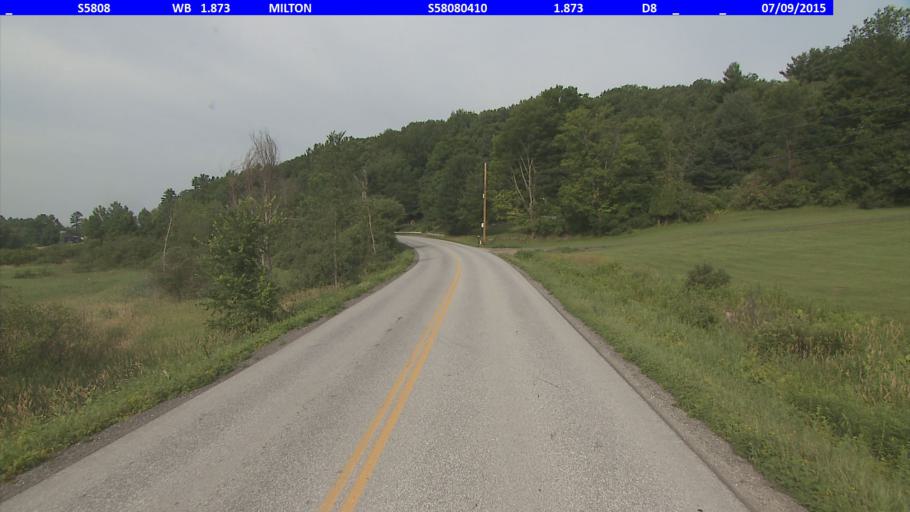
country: US
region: Vermont
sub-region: Chittenden County
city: Milton
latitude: 44.6409
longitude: -73.0801
